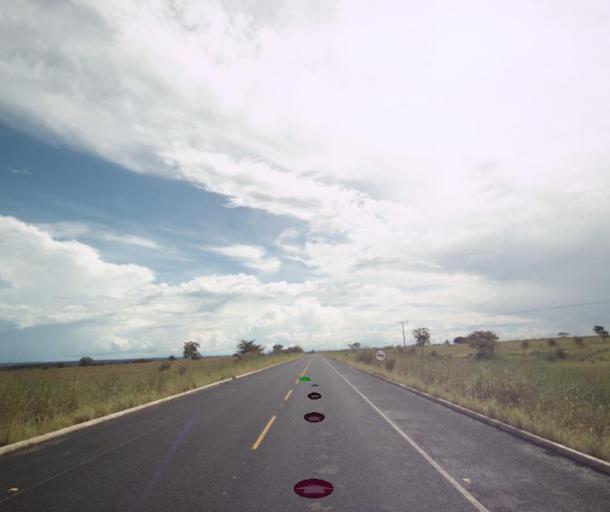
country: BR
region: Goias
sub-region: Sao Miguel Do Araguaia
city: Sao Miguel do Araguaia
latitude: -13.3002
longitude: -50.2577
